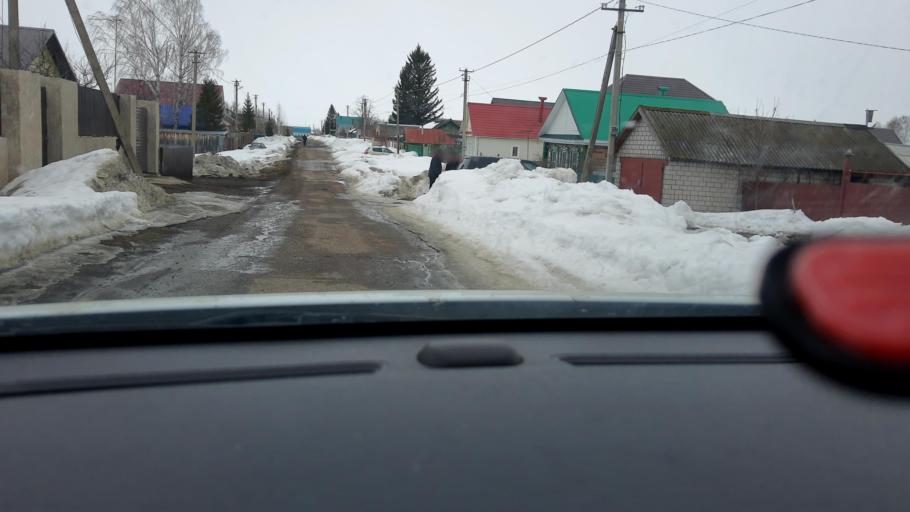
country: RU
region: Bashkortostan
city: Avdon
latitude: 54.4944
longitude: 55.8780
